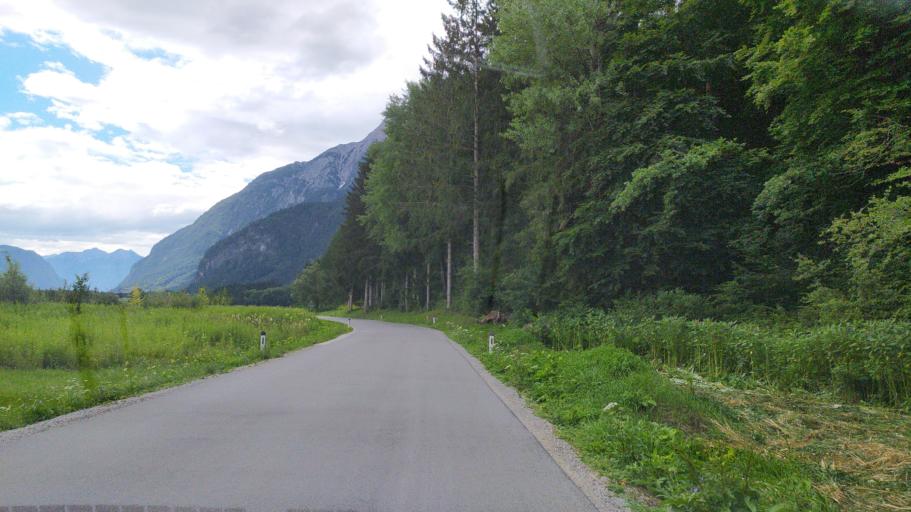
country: AT
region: Tyrol
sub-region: Politischer Bezirk Lienz
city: Lavant
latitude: 46.8070
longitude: 12.8250
